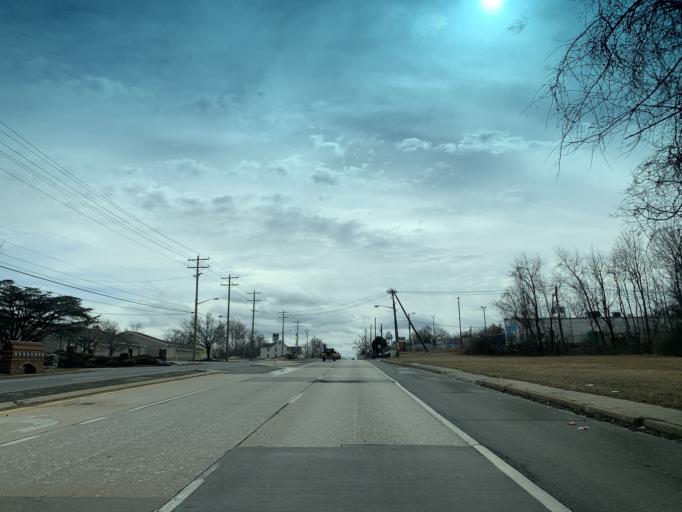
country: US
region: Delaware
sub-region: New Castle County
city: Wilmington
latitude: 39.7106
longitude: -75.5488
